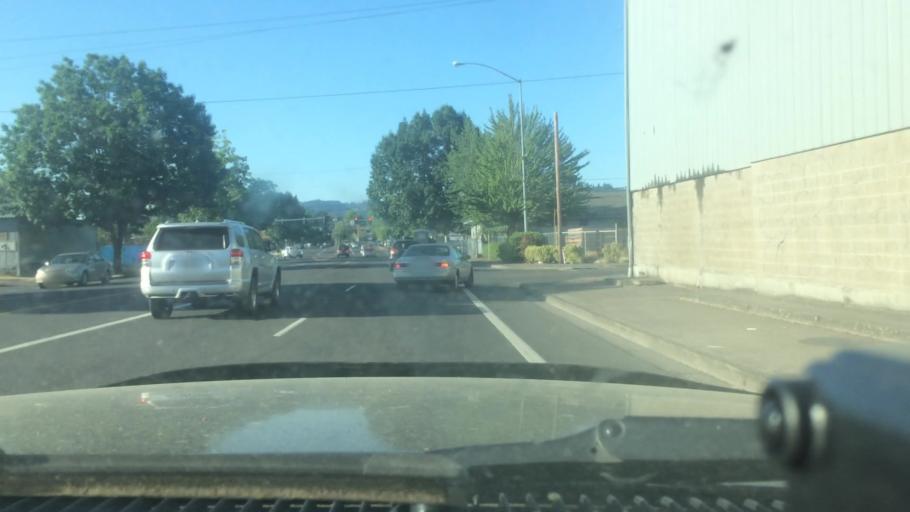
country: US
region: Oregon
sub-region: Lane County
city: Eugene
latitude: 44.0547
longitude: -123.1188
